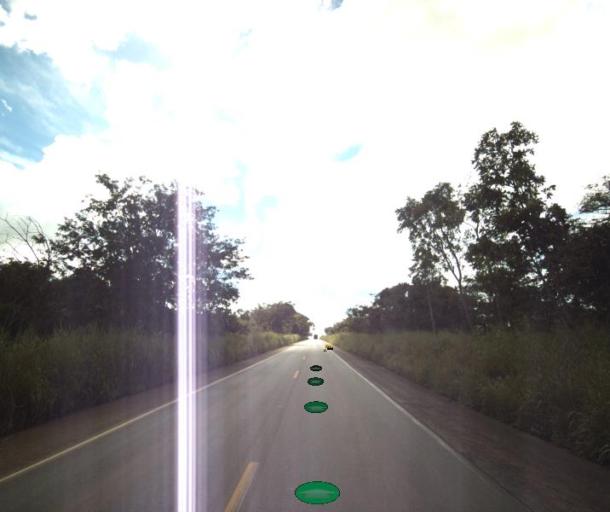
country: BR
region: Goias
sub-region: Jaragua
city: Jaragua
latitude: -15.8642
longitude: -49.2584
